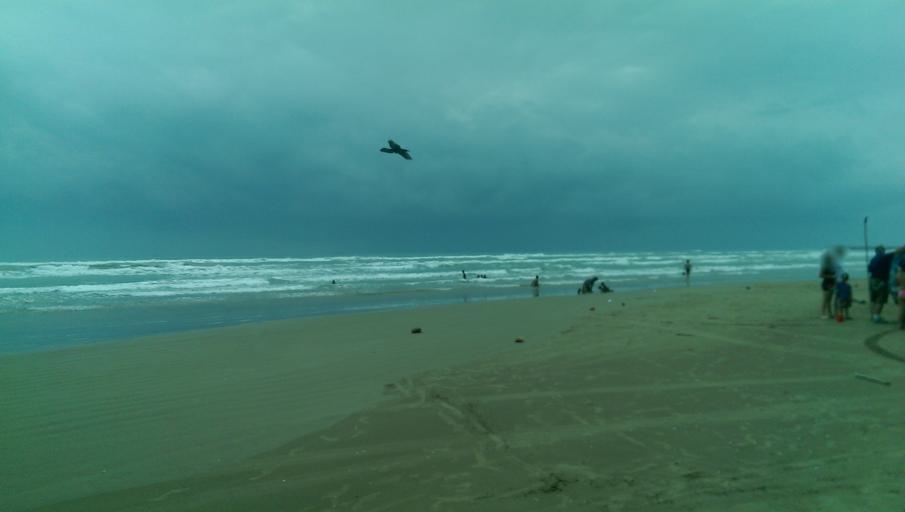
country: MX
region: Veracruz
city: Santiago de la Pena
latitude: 21.0234
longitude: -97.3324
